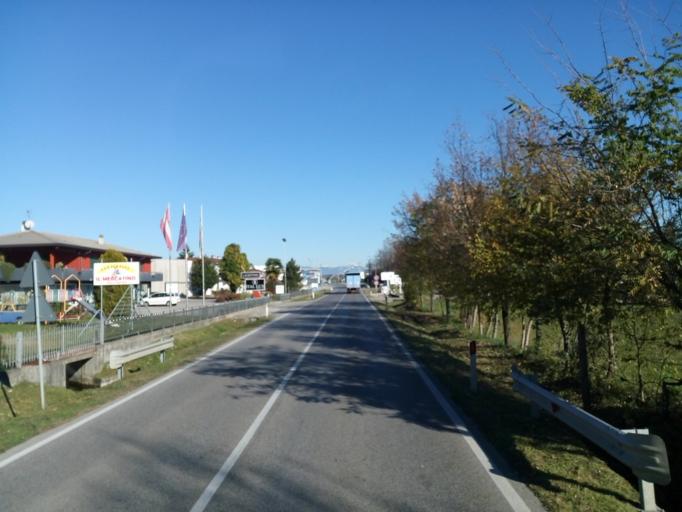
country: IT
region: Veneto
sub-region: Provincia di Treviso
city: Caselle
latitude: 45.7523
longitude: 11.9857
